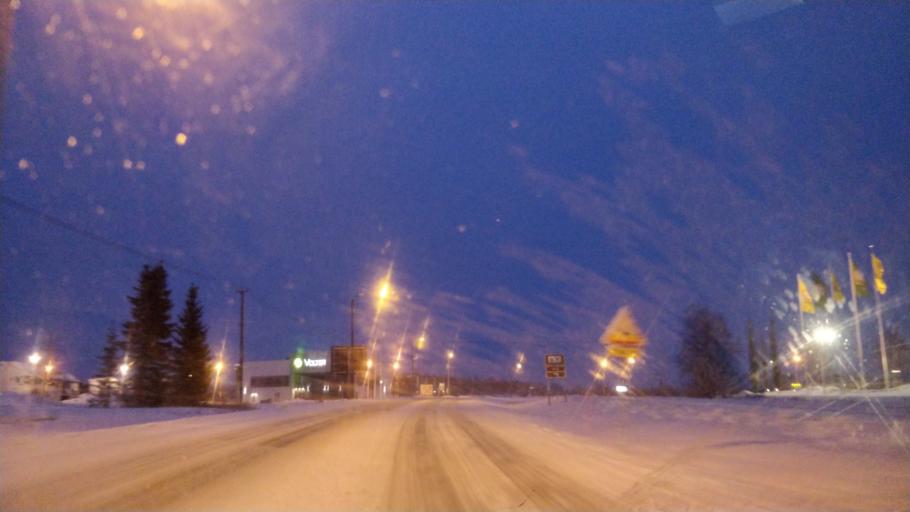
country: FI
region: Northern Ostrobothnia
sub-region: Oulu
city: Kempele
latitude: 64.8636
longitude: 25.5223
